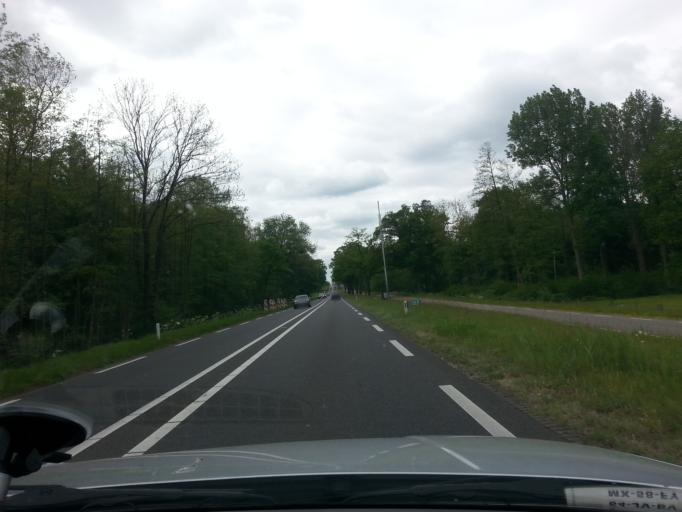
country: NL
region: Overijssel
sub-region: Gemeente Oldenzaal
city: Oldenzaal
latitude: 52.3280
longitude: 6.9476
